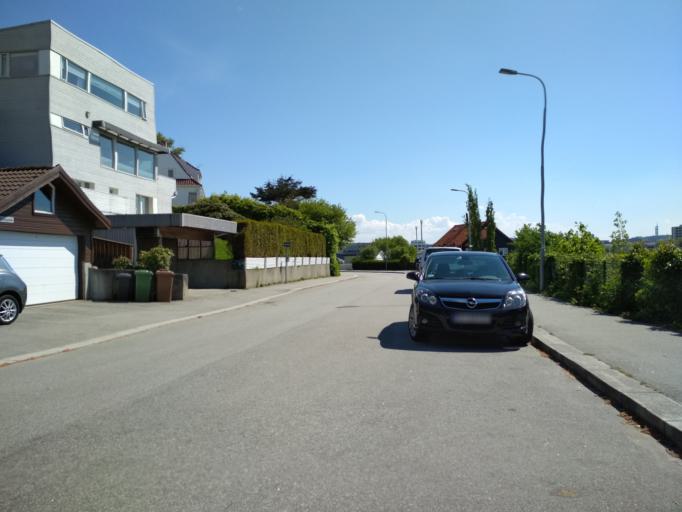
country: NO
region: Rogaland
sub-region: Stavanger
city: Stavanger
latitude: 58.9708
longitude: 5.7063
